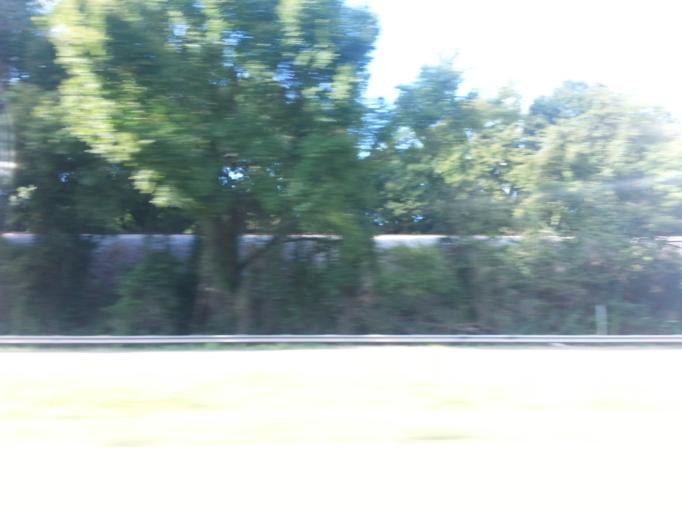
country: US
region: Alabama
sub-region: Colbert County
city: Tuscumbia
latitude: 34.7098
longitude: -87.7574
